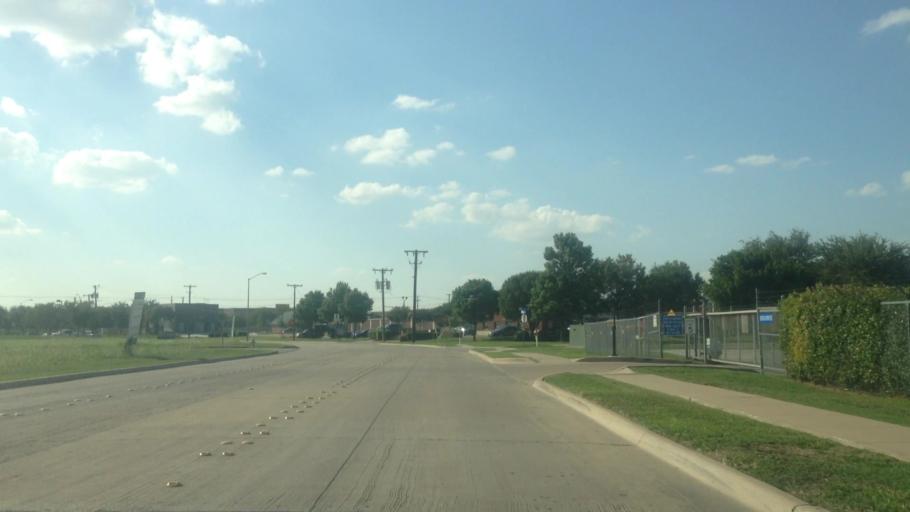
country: US
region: Texas
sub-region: Tarrant County
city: Watauga
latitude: 32.8859
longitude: -97.2573
